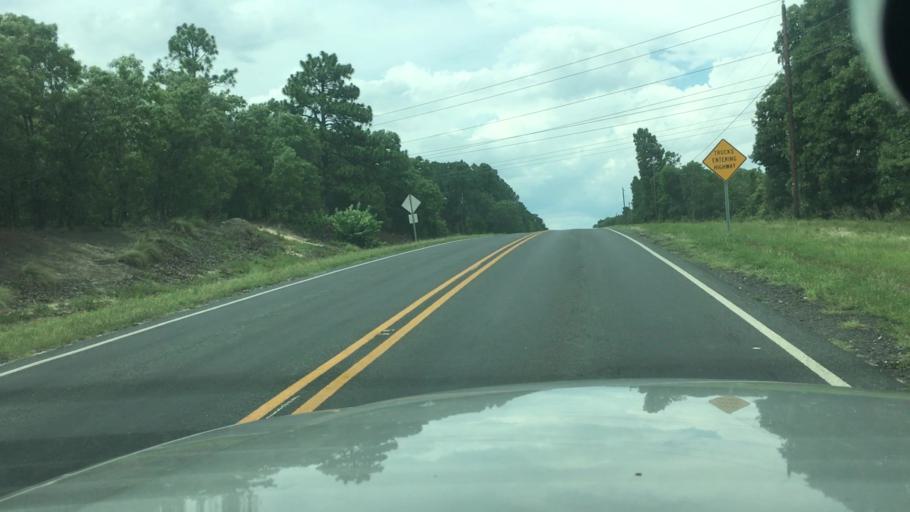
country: US
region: North Carolina
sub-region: Cumberland County
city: Hope Mills
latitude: 34.9658
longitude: -78.8930
